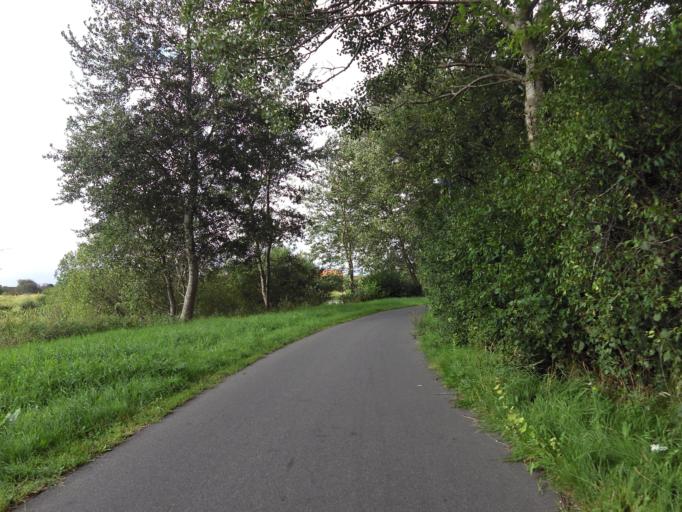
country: DK
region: South Denmark
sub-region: Esbjerg Kommune
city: Ribe
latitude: 55.3342
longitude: 8.7791
